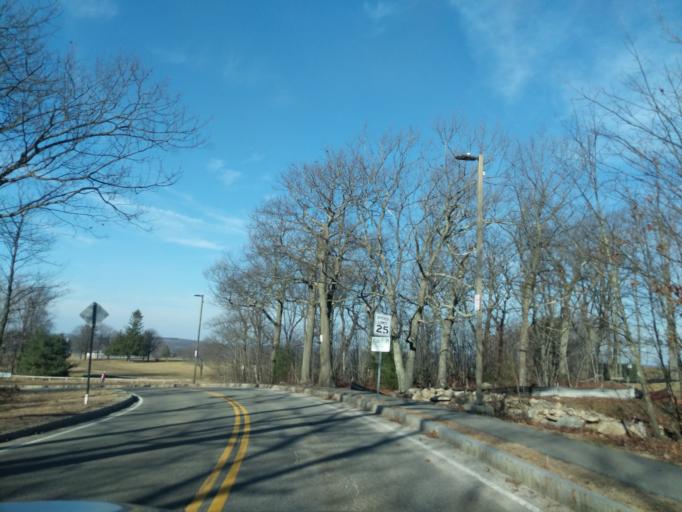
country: US
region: Massachusetts
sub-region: Worcester County
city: Hamilton
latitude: 42.2827
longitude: -71.7751
